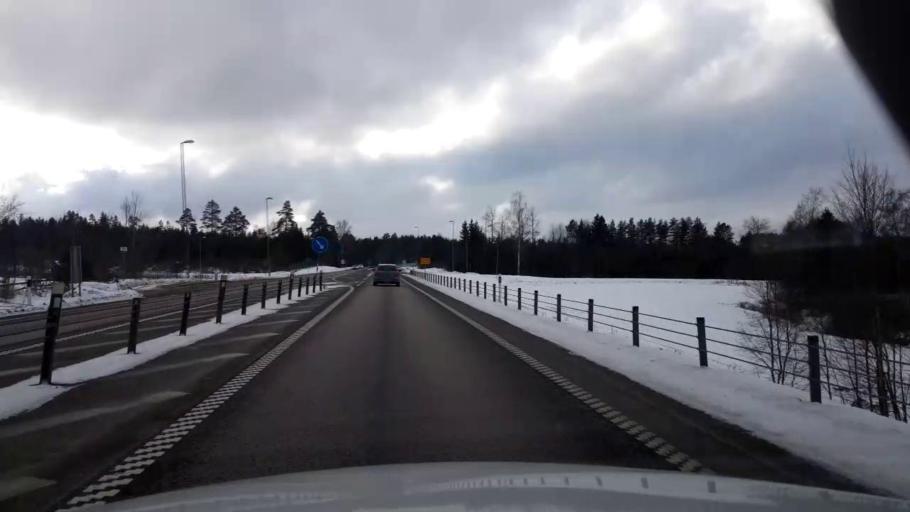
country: SE
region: Gaevleborg
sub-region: Hudiksvalls Kommun
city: Hudiksvall
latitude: 61.8002
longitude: 17.1719
